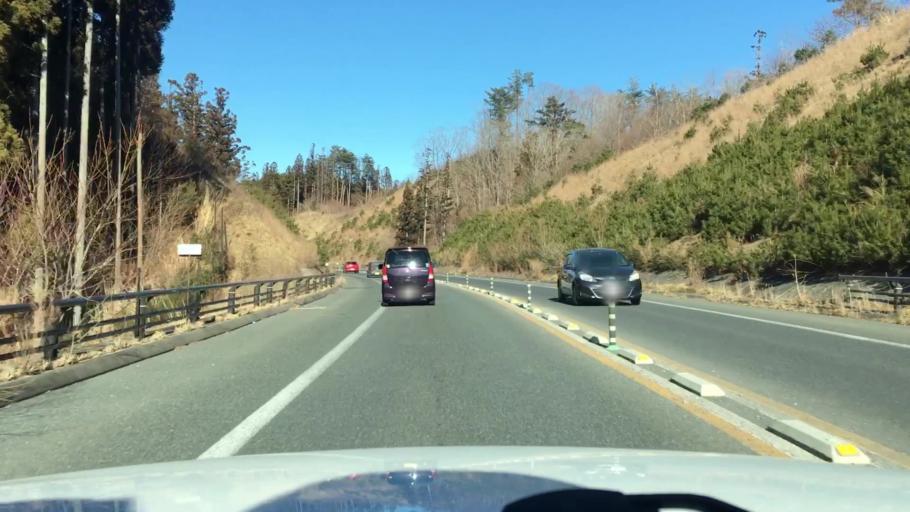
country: JP
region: Iwate
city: Miyako
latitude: 39.6117
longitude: 141.9344
